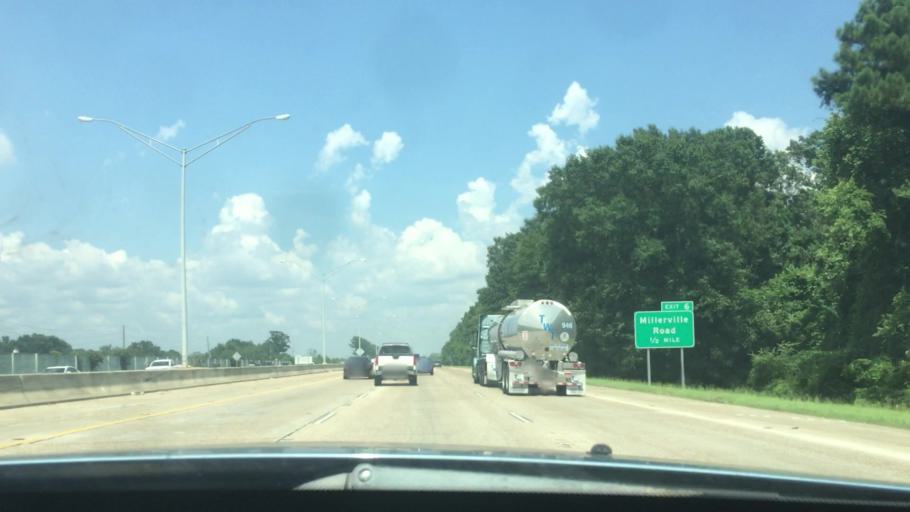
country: US
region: Louisiana
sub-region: East Baton Rouge Parish
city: Shenandoah
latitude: 30.4343
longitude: -91.0396
